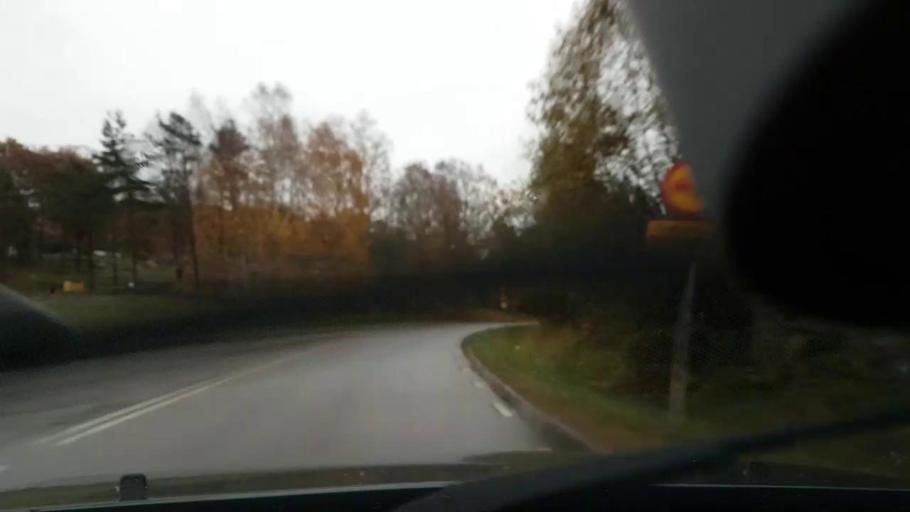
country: SE
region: Vaestra Goetaland
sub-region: Molndal
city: Kallered
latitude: 57.6028
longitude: 12.0780
